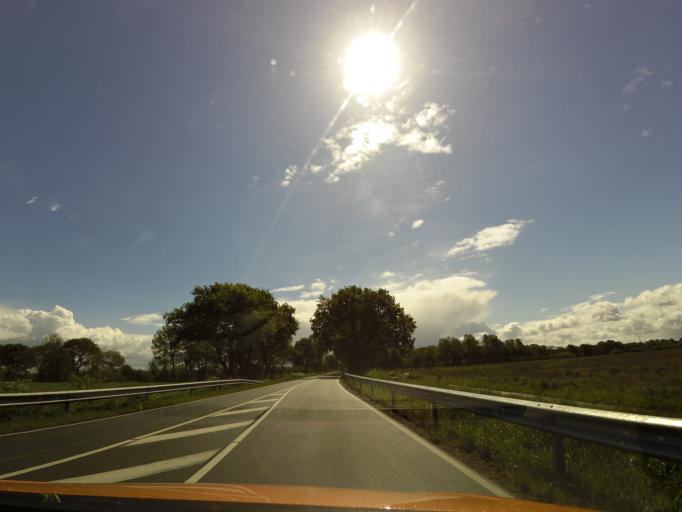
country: DE
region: Lower Saxony
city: Oldenburg
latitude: 53.1313
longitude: 8.2926
